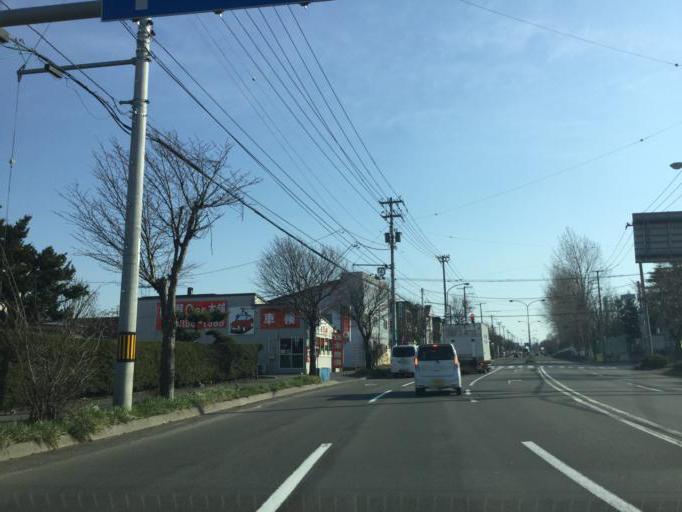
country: JP
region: Hokkaido
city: Ebetsu
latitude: 43.0748
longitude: 141.4847
